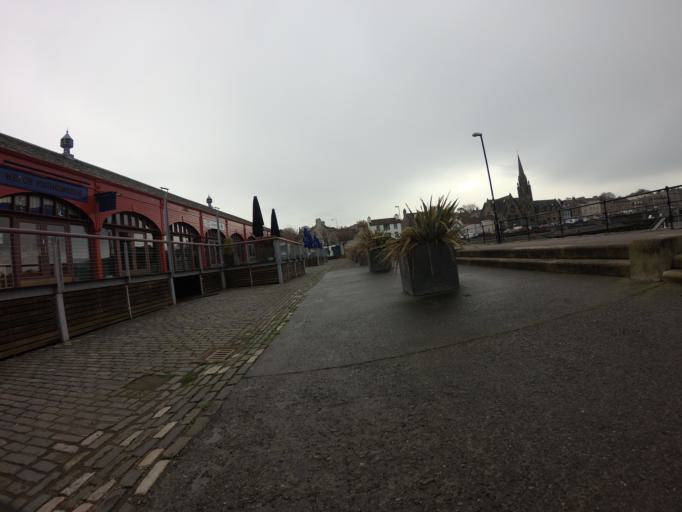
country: GB
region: Scotland
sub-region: Edinburgh
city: Edinburgh
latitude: 55.9812
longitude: -3.1951
